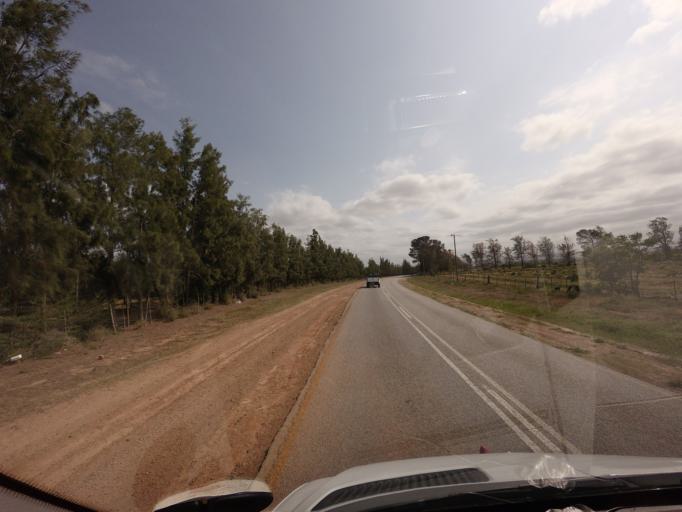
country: ZA
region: Eastern Cape
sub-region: Cacadu District Municipality
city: Kirkwood
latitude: -33.5652
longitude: 25.6805
